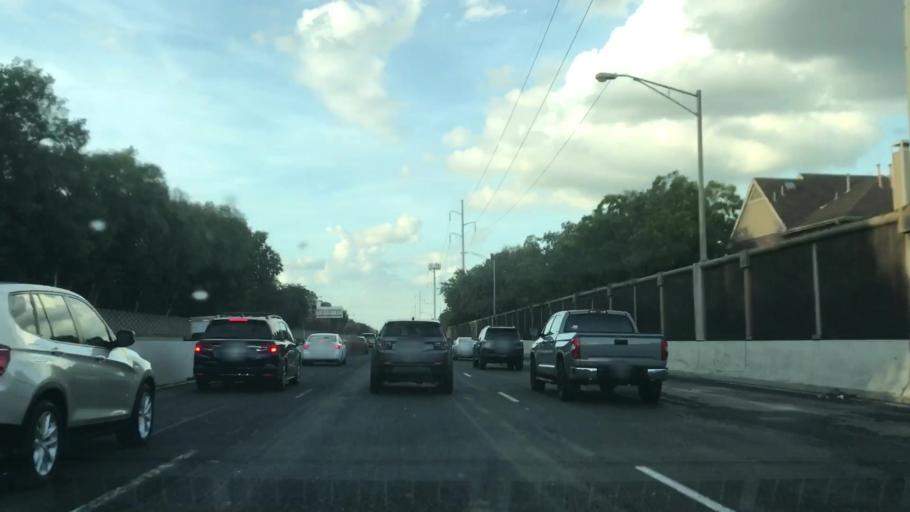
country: US
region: Texas
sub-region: Dallas County
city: University Park
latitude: 32.8401
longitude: -96.8145
